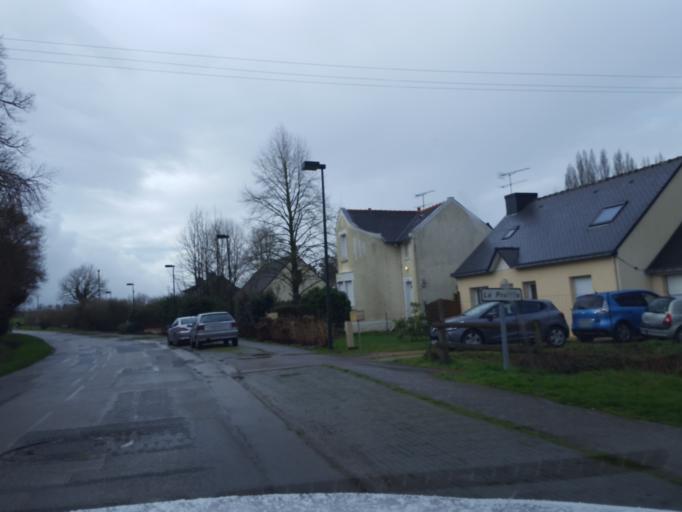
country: FR
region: Brittany
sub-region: Departement d'Ille-et-Vilaine
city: Guignen
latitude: 47.9174
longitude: -1.8610
